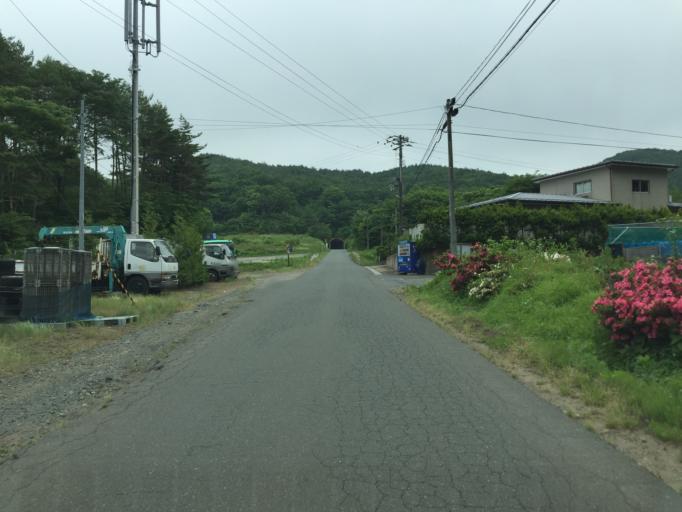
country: JP
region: Fukushima
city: Yanagawamachi-saiwaicho
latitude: 37.7764
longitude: 140.7130
